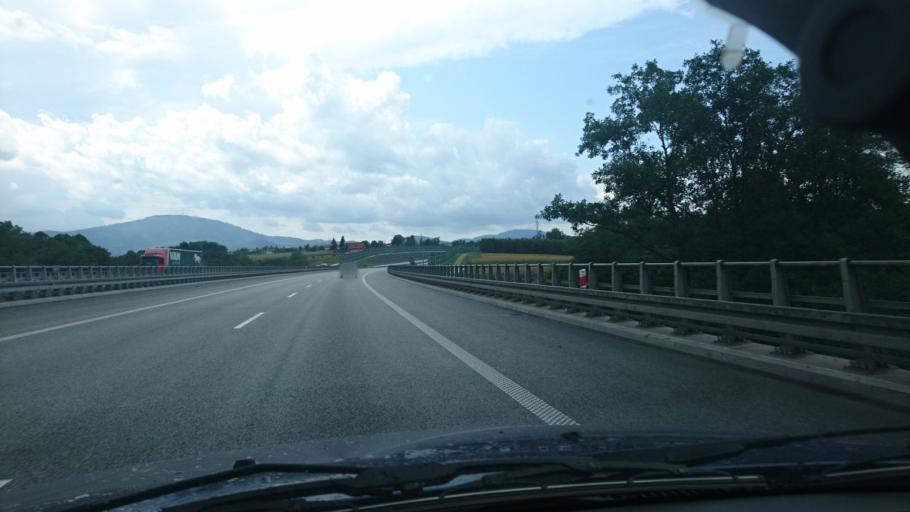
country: PL
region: Silesian Voivodeship
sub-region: Powiat zywiecki
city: Pietrzykowice
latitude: 49.6852
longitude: 19.1471
